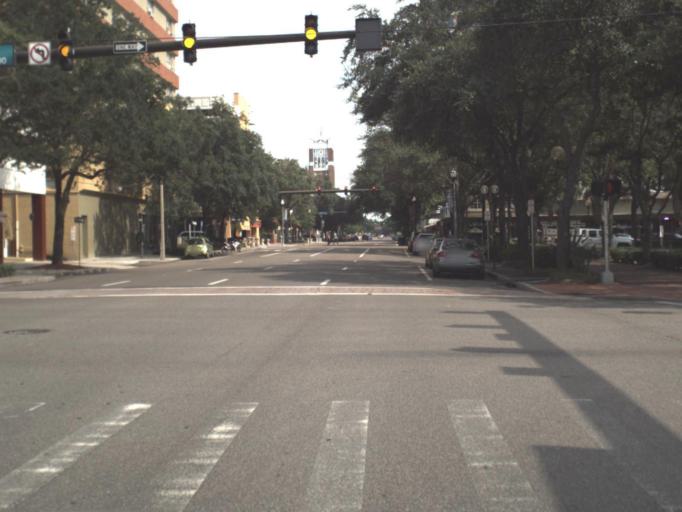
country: US
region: Florida
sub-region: Pinellas County
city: Saint Petersburg
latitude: 27.7702
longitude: -82.6370
